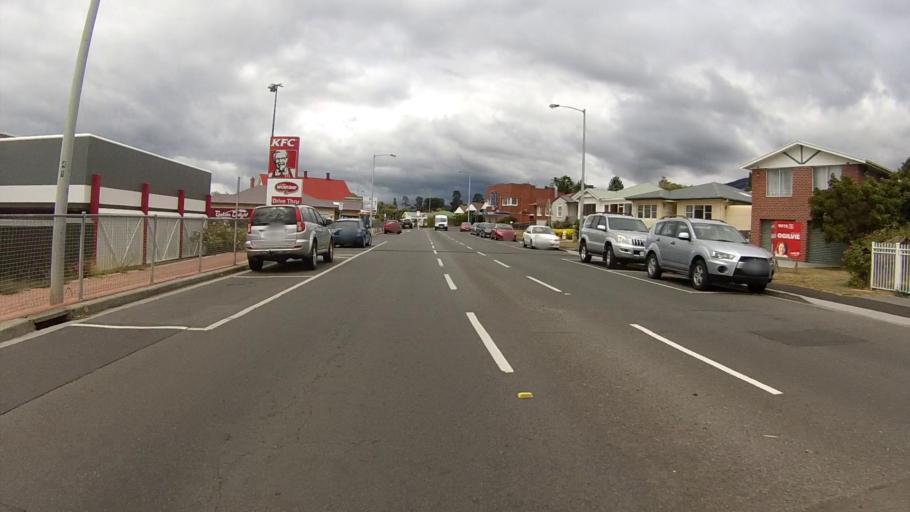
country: AU
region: Tasmania
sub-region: Glenorchy
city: Claremont
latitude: -42.7901
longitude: 147.2536
